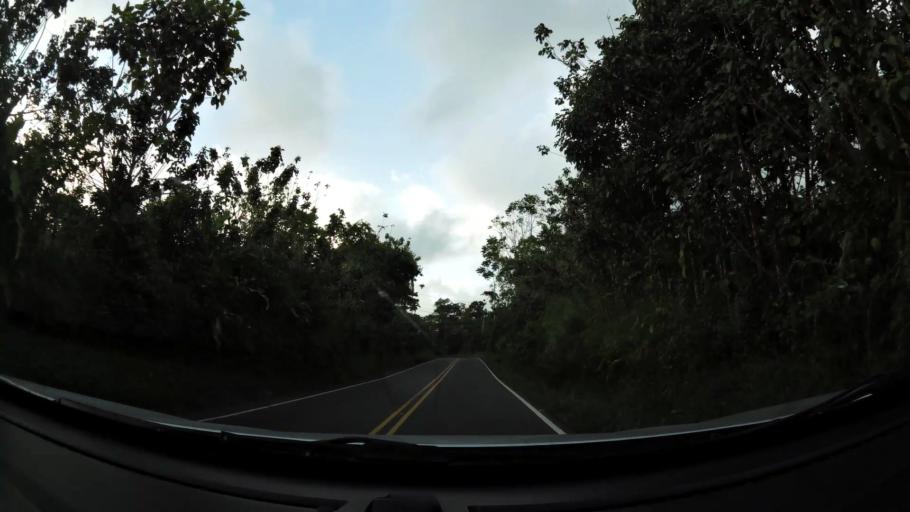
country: CR
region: Limon
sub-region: Canton de Siquirres
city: Siquirres
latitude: 9.9818
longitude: -83.5707
